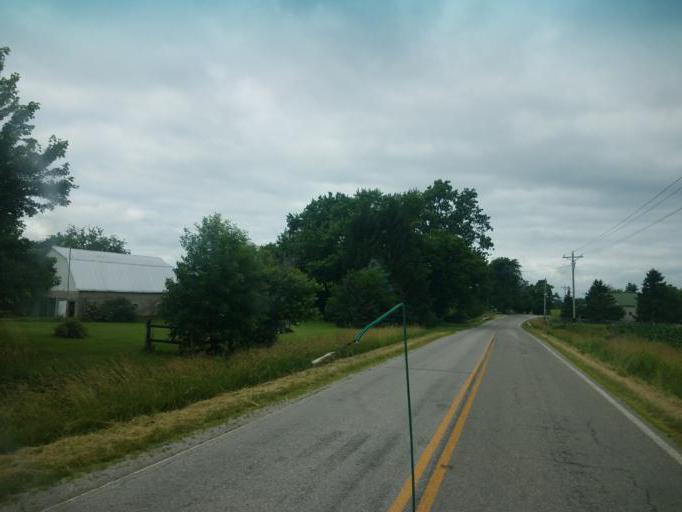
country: US
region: Ohio
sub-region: Champaign County
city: North Lewisburg
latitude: 40.4114
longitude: -83.4970
